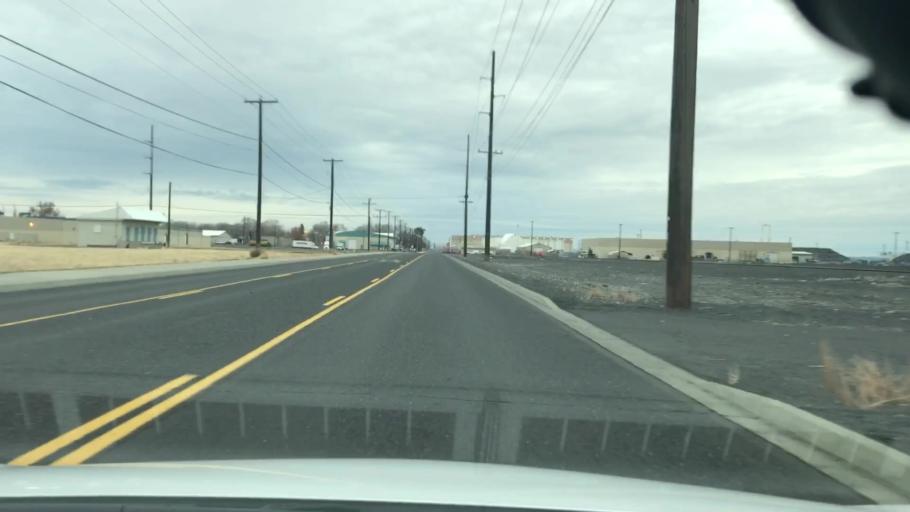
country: US
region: Washington
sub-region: Grant County
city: Moses Lake North
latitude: 47.1788
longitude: -119.3165
